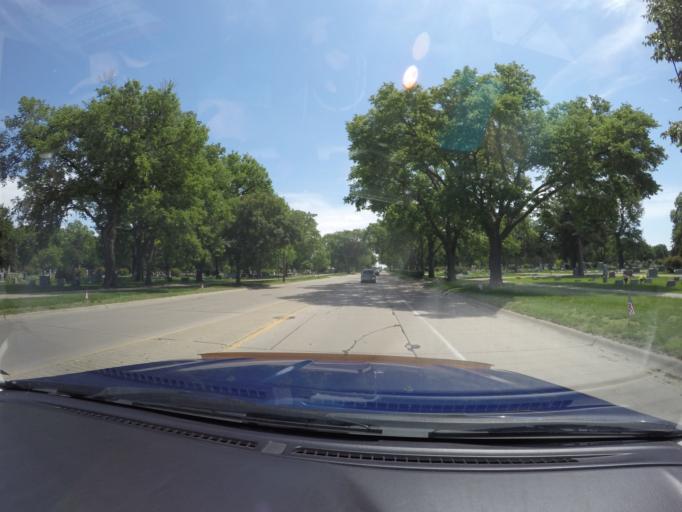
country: US
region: Nebraska
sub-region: Hall County
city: Grand Island
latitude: 40.9026
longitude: -98.3774
